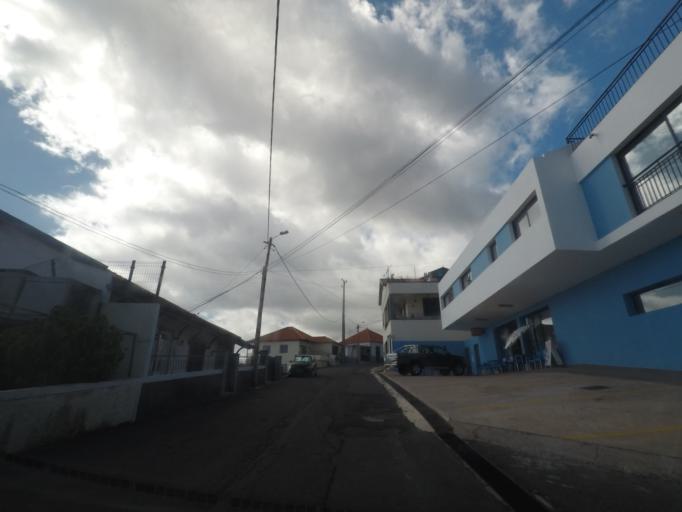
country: PT
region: Madeira
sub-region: Ribeira Brava
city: Campanario
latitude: 32.6686
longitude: -17.0499
